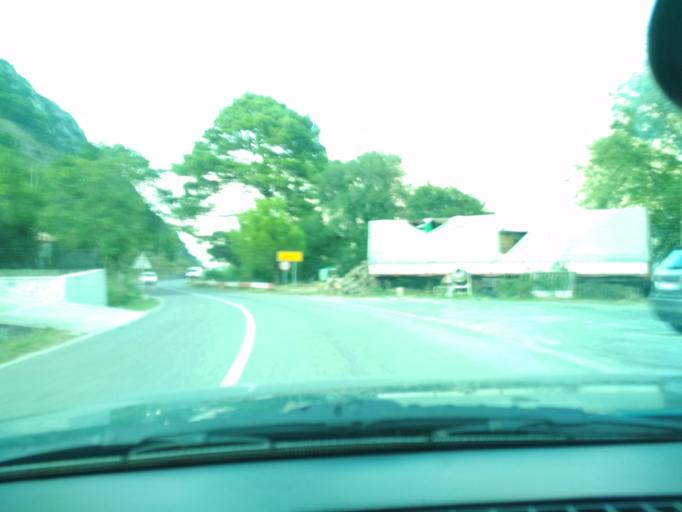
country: ME
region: Kotor
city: Kotor
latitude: 42.4040
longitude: 18.7643
